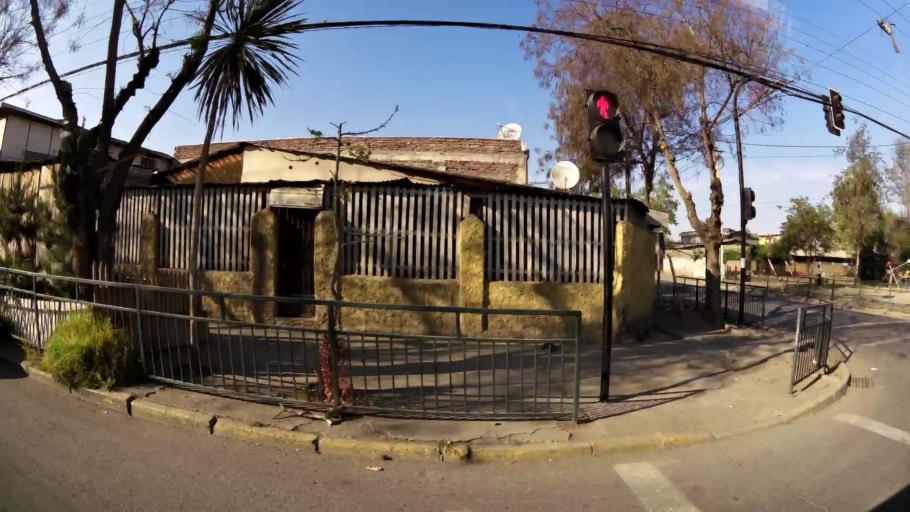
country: CL
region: Santiago Metropolitan
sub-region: Provincia de Santiago
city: Santiago
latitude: -33.3811
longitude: -70.6491
